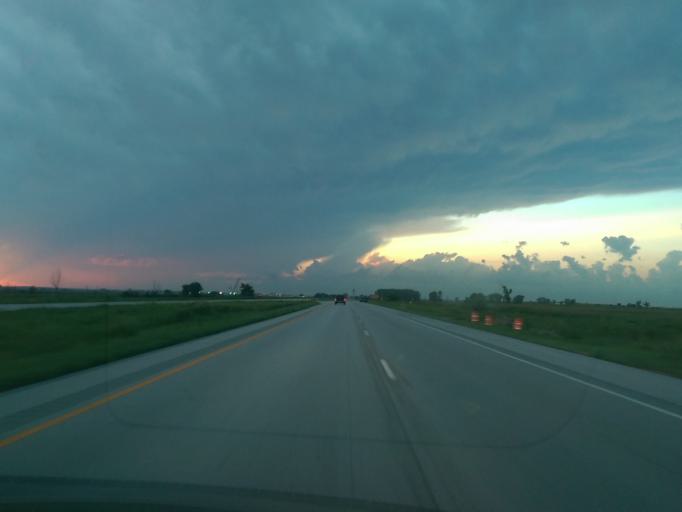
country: US
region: Nebraska
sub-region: Otoe County
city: Nebraska City
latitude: 40.6742
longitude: -95.7701
